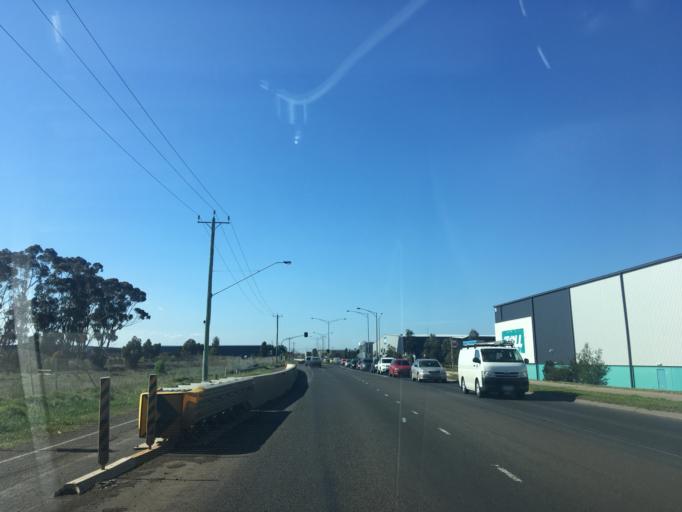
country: AU
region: Victoria
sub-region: Wyndham
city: Truganina
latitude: -37.8173
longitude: 144.7500
